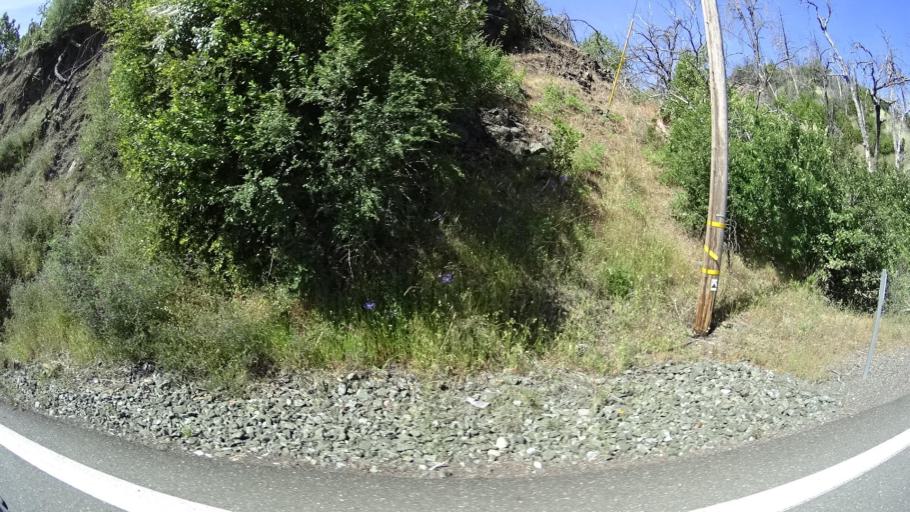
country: US
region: California
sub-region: Lake County
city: Cobb
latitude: 38.7853
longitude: -122.6923
